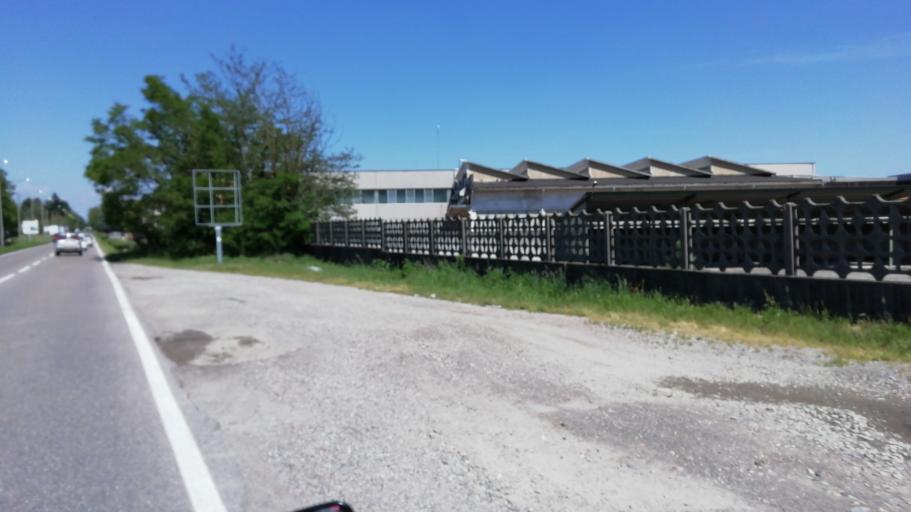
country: IT
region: Lombardy
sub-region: Provincia di Varese
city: Lonate Pozzolo
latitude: 45.5911
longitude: 8.7363
